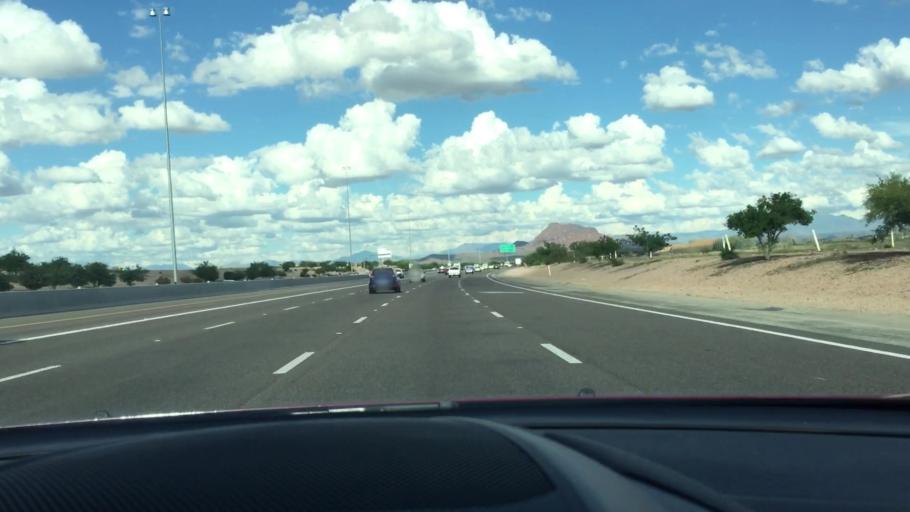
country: US
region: Arizona
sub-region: Maricopa County
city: Mesa
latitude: 33.4617
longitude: -111.7499
